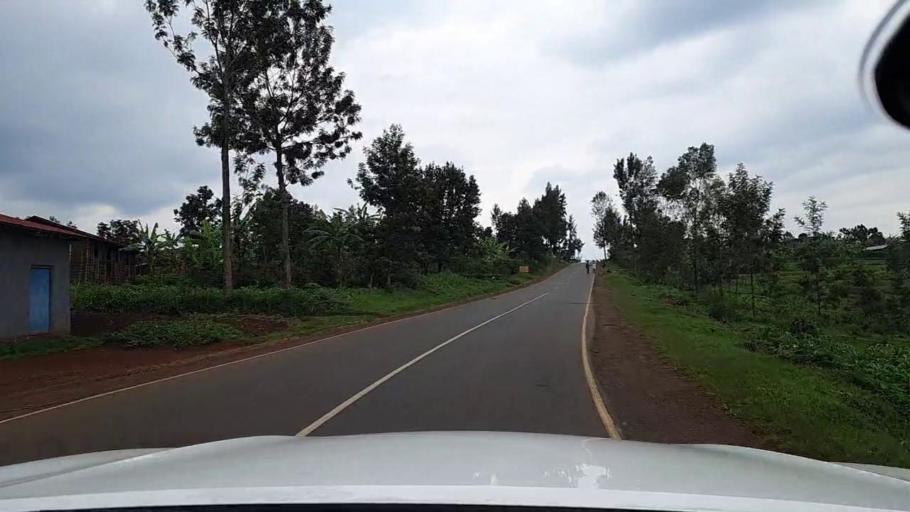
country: RW
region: Western Province
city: Cyangugu
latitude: -2.5937
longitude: 28.9305
